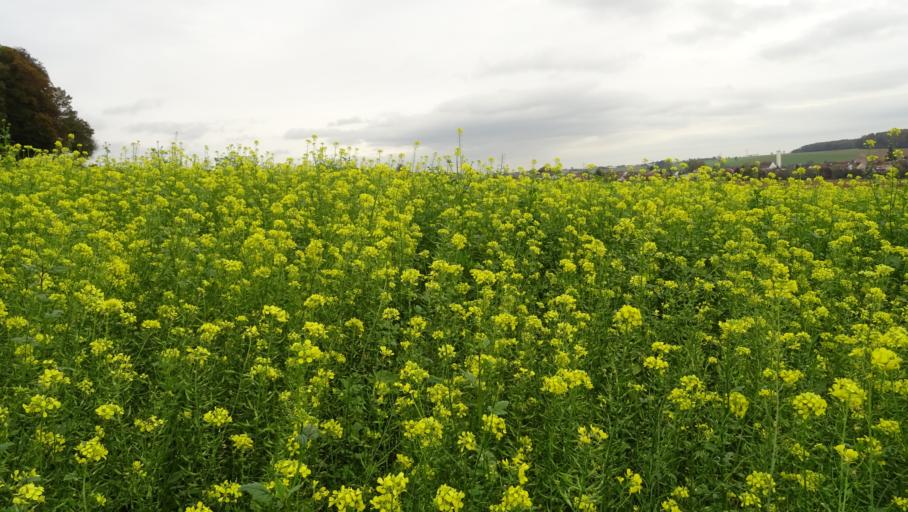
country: DE
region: Baden-Wuerttemberg
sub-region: Karlsruhe Region
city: Neckargerach
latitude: 49.3978
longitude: 9.0865
